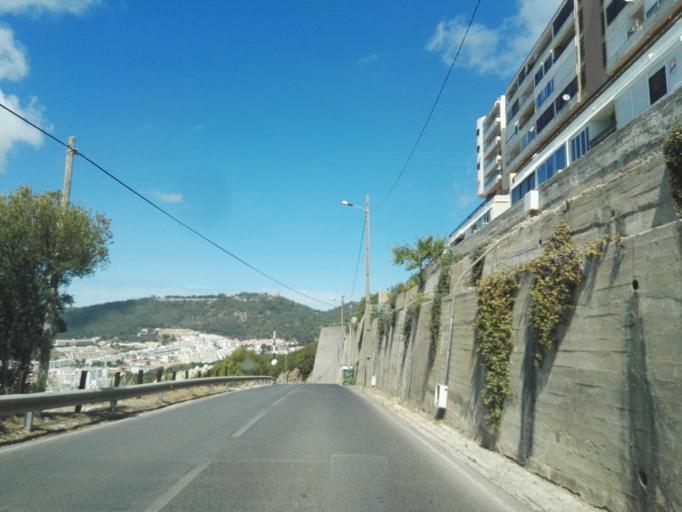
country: PT
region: Setubal
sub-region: Sesimbra
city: Sesimbra
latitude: 38.4422
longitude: -9.0907
